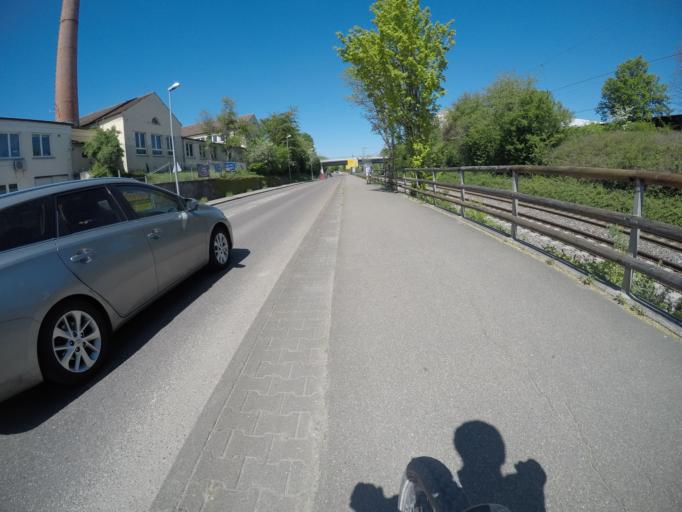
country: DE
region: Baden-Wuerttemberg
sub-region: Regierungsbezirk Stuttgart
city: Waiblingen
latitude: 48.8205
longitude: 9.3131
